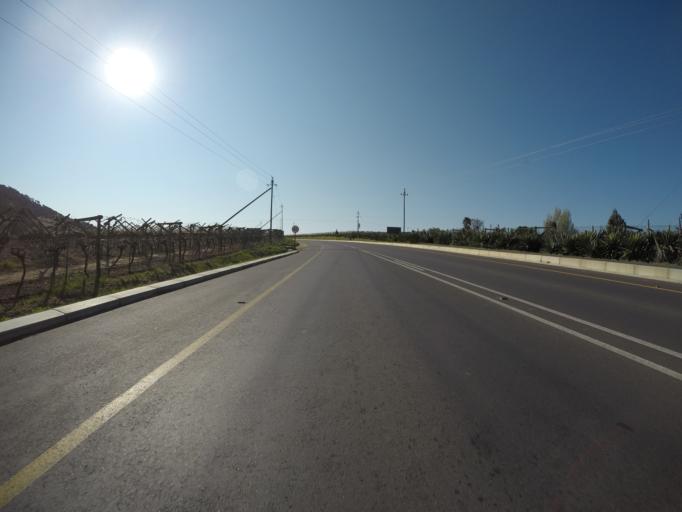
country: ZA
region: Western Cape
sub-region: Cape Winelands District Municipality
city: Noorder-Paarl
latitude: -33.6948
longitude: 18.9580
